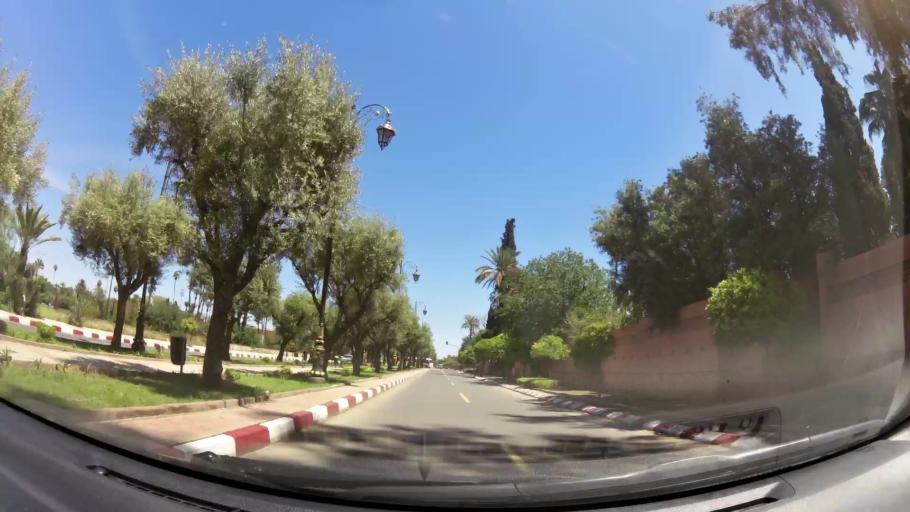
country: MA
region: Marrakech-Tensift-Al Haouz
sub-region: Marrakech
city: Marrakesh
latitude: 31.6254
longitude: -8.0108
